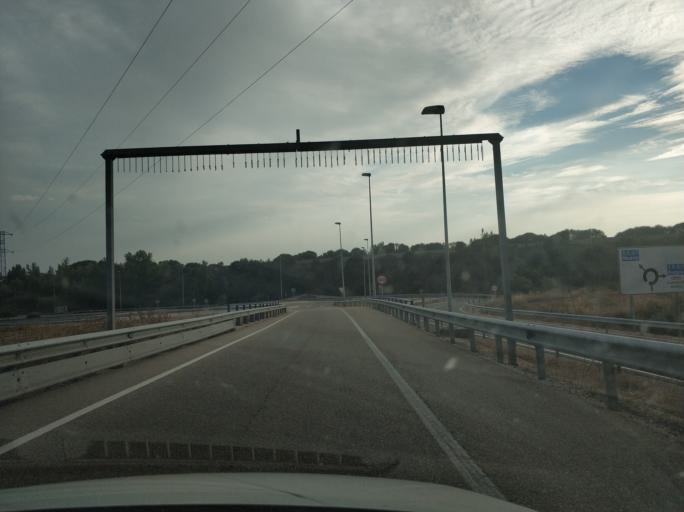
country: ES
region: Castille and Leon
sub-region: Provincia de Burgos
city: Saldana de Burgos
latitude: 42.2656
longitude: -3.6997
